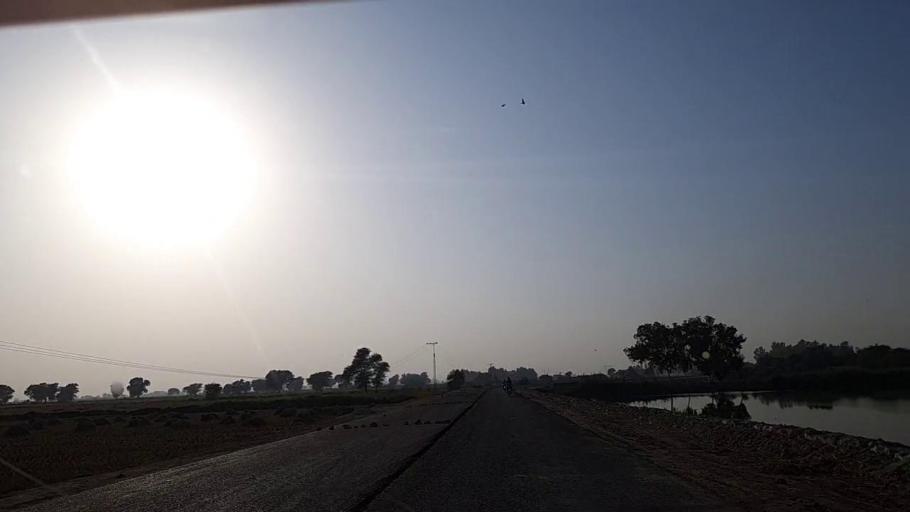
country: PK
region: Sindh
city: Rustam jo Goth
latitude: 27.9636
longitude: 68.8047
